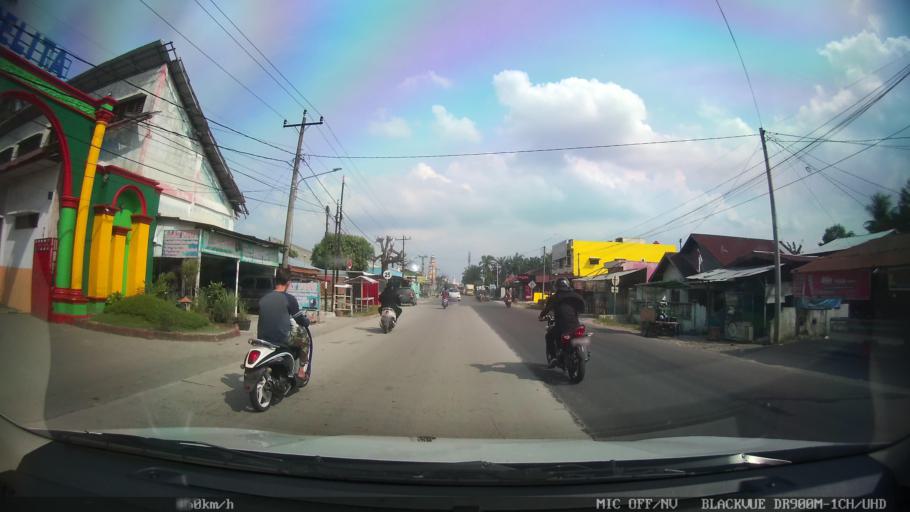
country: ID
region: North Sumatra
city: Binjai
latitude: 3.6293
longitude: 98.4927
